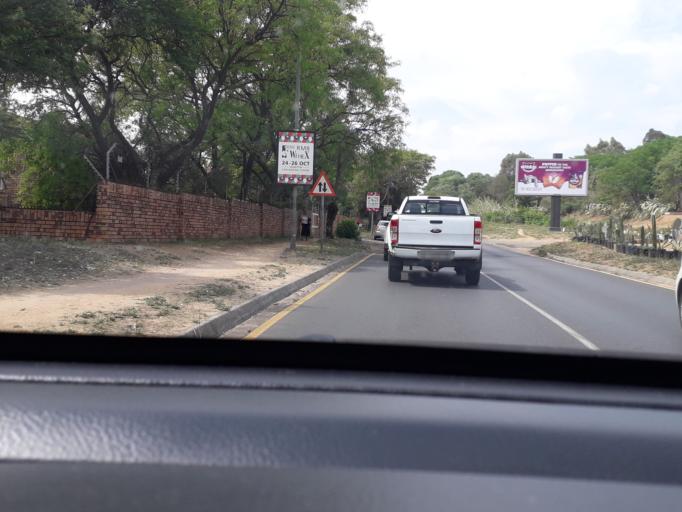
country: ZA
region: Gauteng
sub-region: City of Johannesburg Metropolitan Municipality
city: Midrand
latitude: -26.0676
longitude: 28.0624
